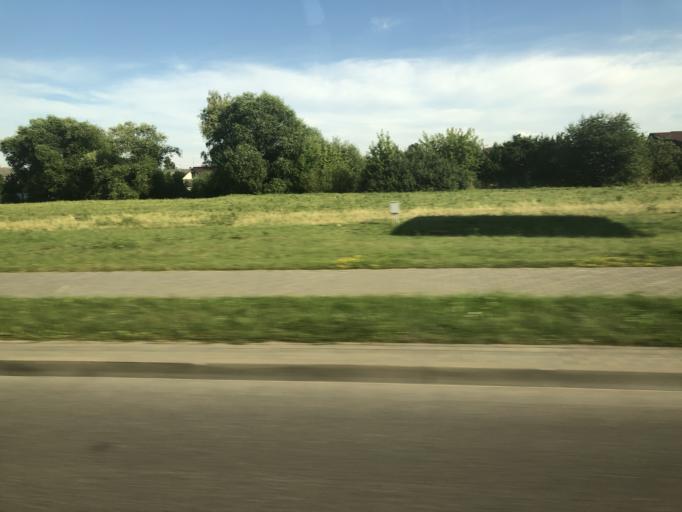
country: BY
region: Grodnenskaya
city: Hrodna
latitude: 53.6499
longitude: 23.7844
